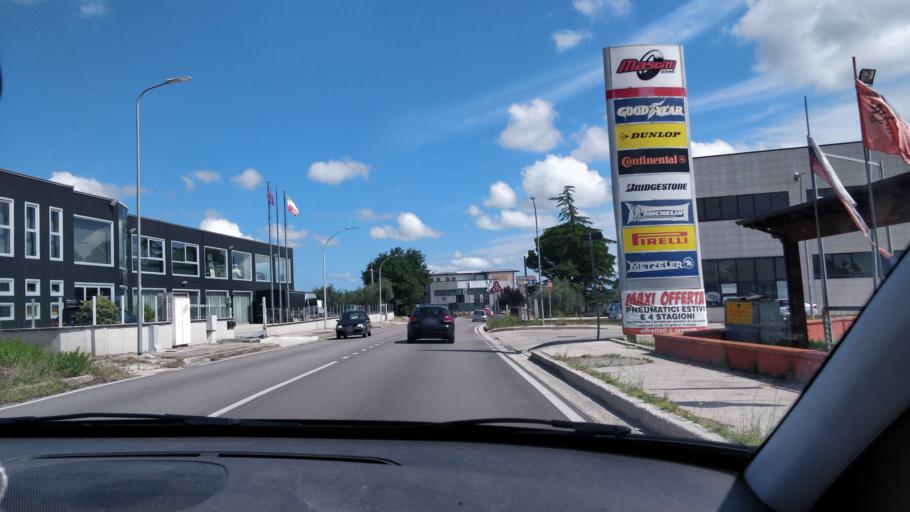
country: IT
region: Abruzzo
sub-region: Provincia di Chieti
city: Lanciano
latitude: 42.2401
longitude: 14.4100
